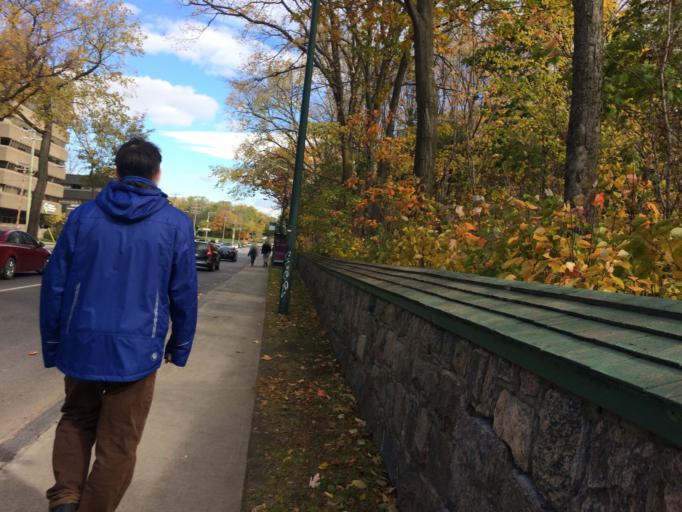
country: CA
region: Quebec
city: Quebec
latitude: 46.7898
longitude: -71.2450
